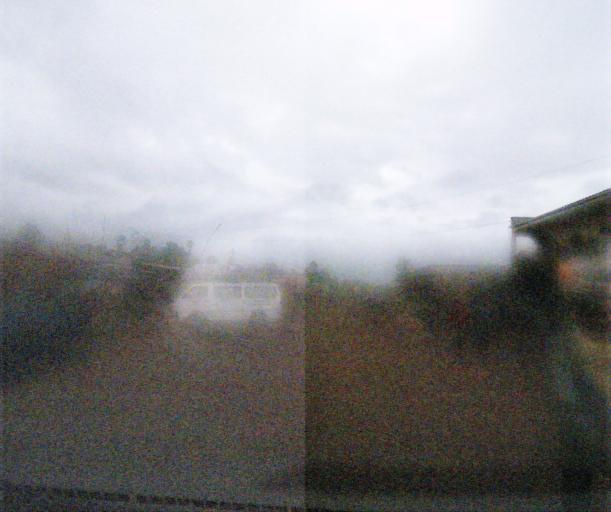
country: CM
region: West
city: Bansoa
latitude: 5.5011
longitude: 10.2425
